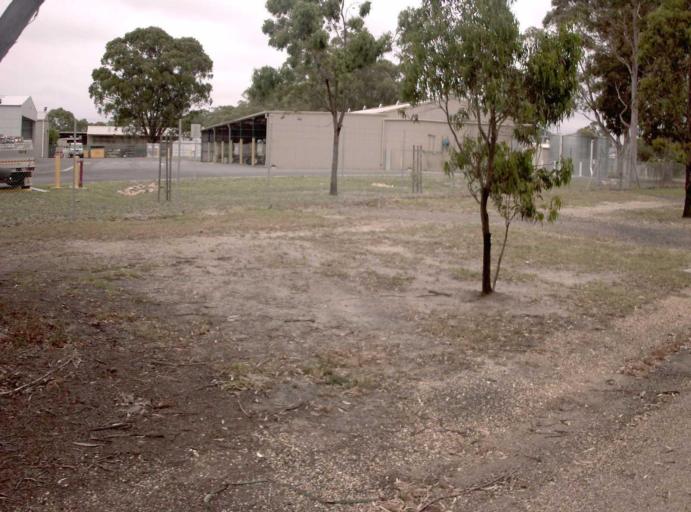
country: AU
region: Victoria
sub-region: Wellington
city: Heyfield
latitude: -37.9770
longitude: 146.7833
